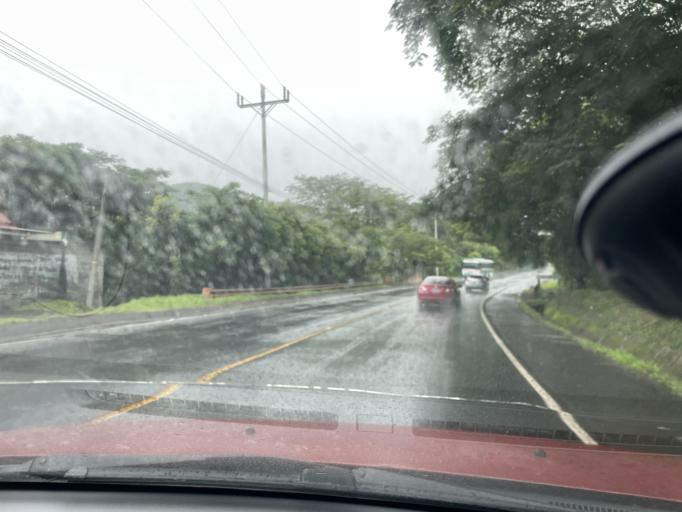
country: SV
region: San Miguel
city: San Miguel
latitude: 13.5510
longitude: -88.1178
